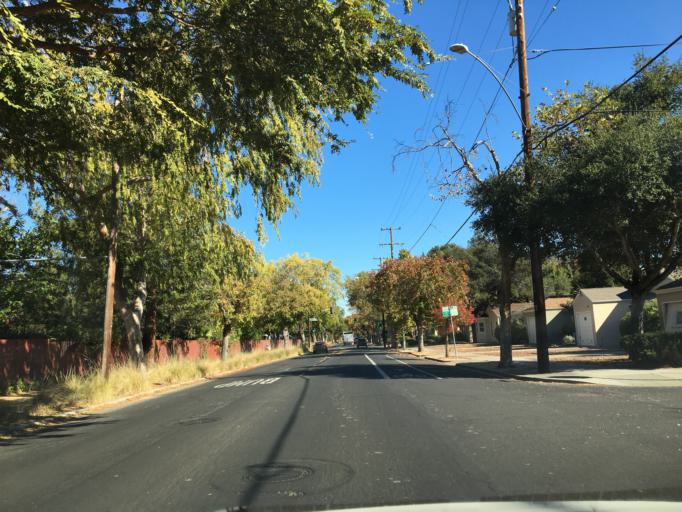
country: US
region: California
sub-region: Santa Clara County
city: Stanford
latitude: 37.4204
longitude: -122.1553
